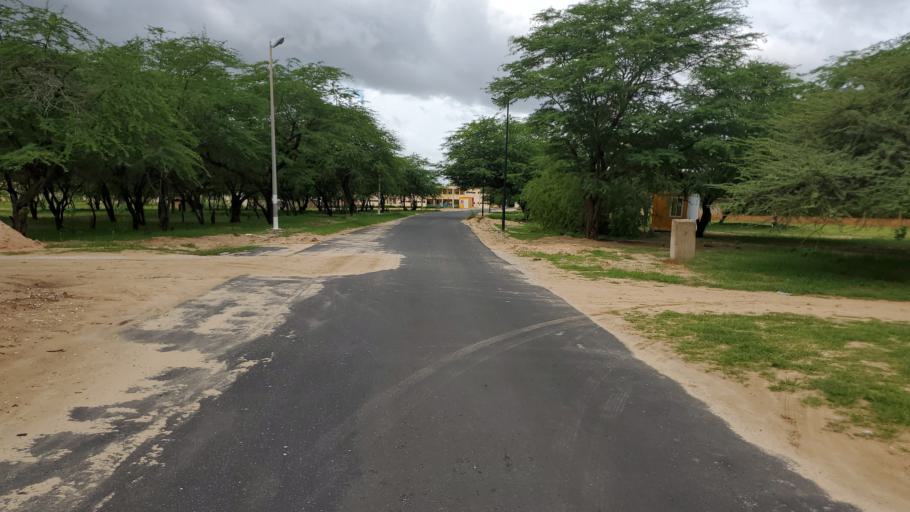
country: SN
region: Saint-Louis
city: Saint-Louis
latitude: 16.0635
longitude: -16.4282
